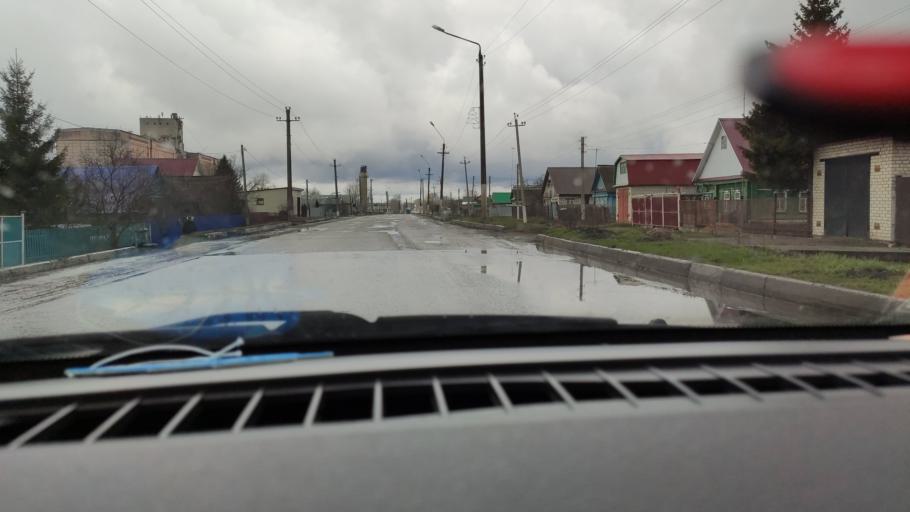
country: RU
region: Tatarstan
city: Nurlat
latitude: 54.4286
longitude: 50.8188
